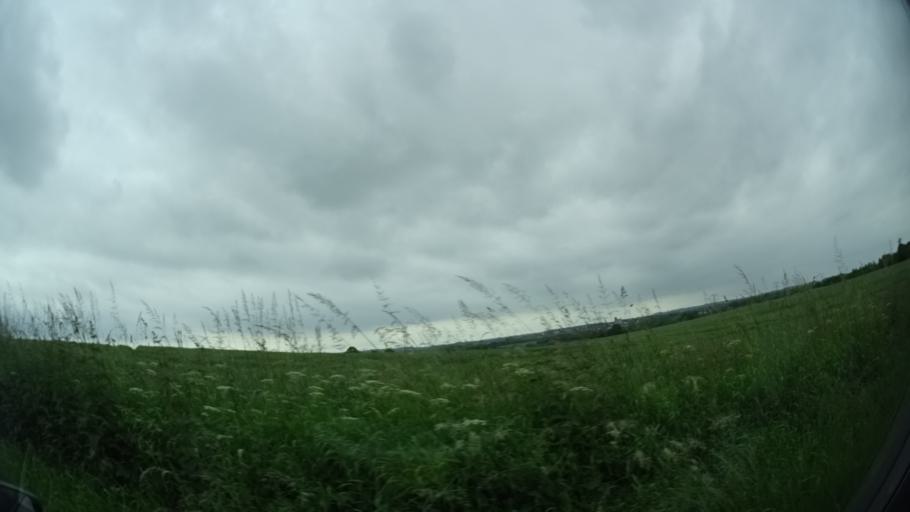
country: DK
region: Central Jutland
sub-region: Arhus Kommune
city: Kolt
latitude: 56.0894
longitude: 10.0771
